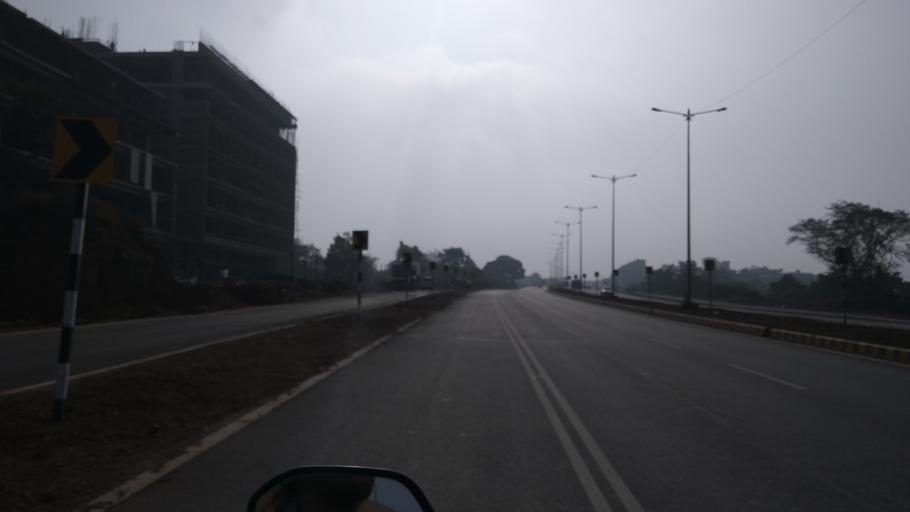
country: IN
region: Goa
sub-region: North Goa
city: Bambolim
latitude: 15.4988
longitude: 73.8755
